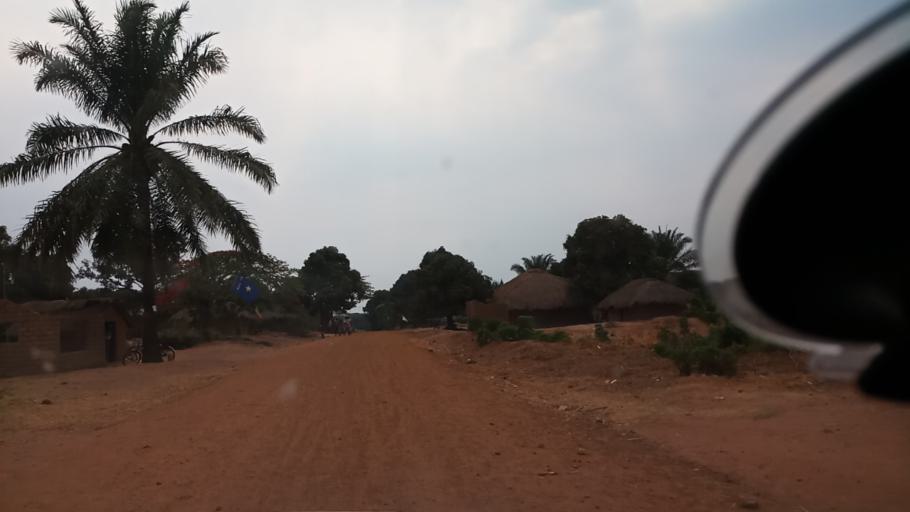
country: ZM
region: Luapula
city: Nchelenge
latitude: -9.0999
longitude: 28.3010
